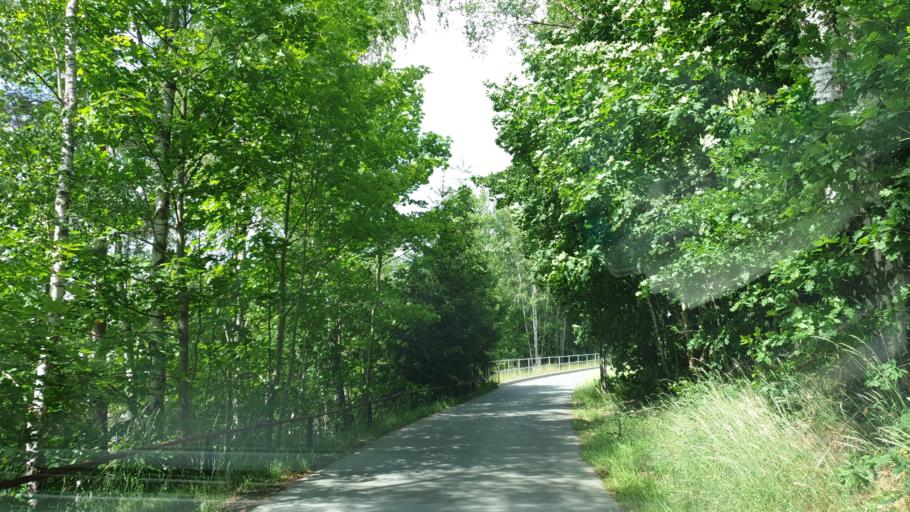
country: DE
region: Saxony
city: Adorf
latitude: 50.3331
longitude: 12.2579
